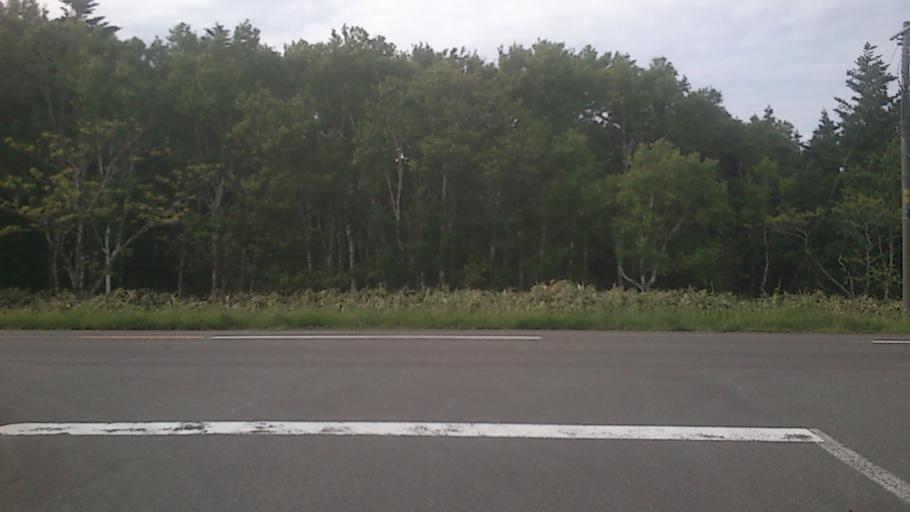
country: JP
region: Hokkaido
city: Makubetsu
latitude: 45.1124
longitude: 141.7041
